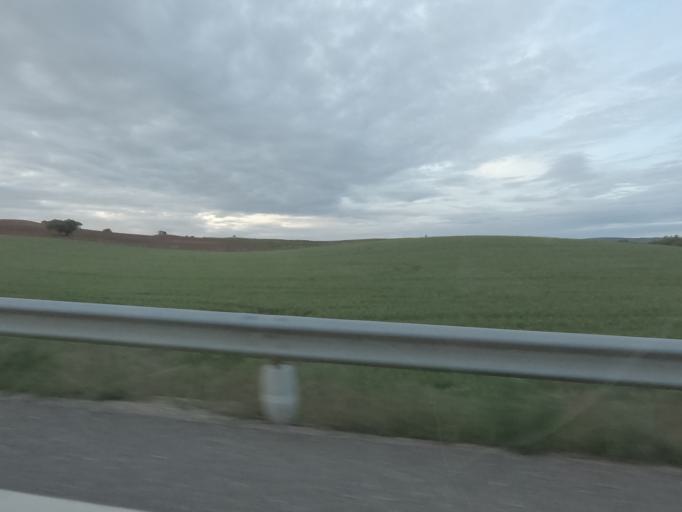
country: ES
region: Extremadura
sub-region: Provincia de Badajoz
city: La Roca de la Sierra
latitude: 39.0574
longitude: -6.7773
